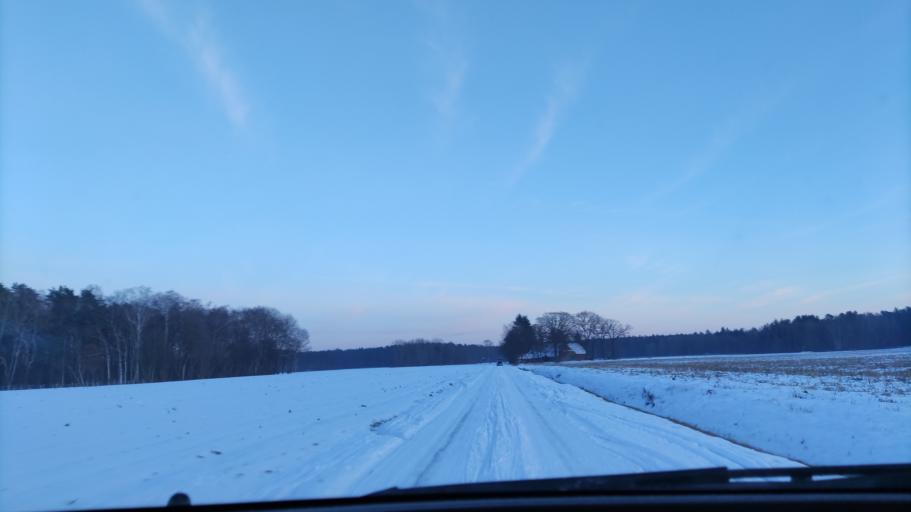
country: DE
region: Lower Saxony
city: Bleckede
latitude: 53.2917
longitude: 10.6776
